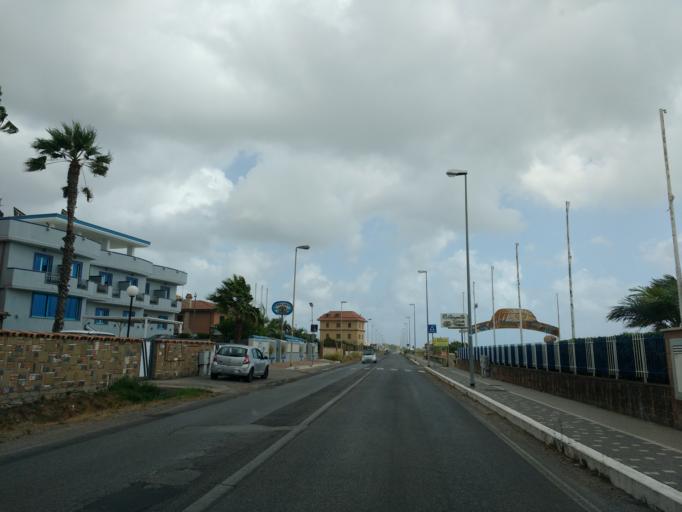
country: IT
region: Latium
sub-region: Citta metropolitana di Roma Capitale
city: Anzio
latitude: 41.4747
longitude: 12.6036
